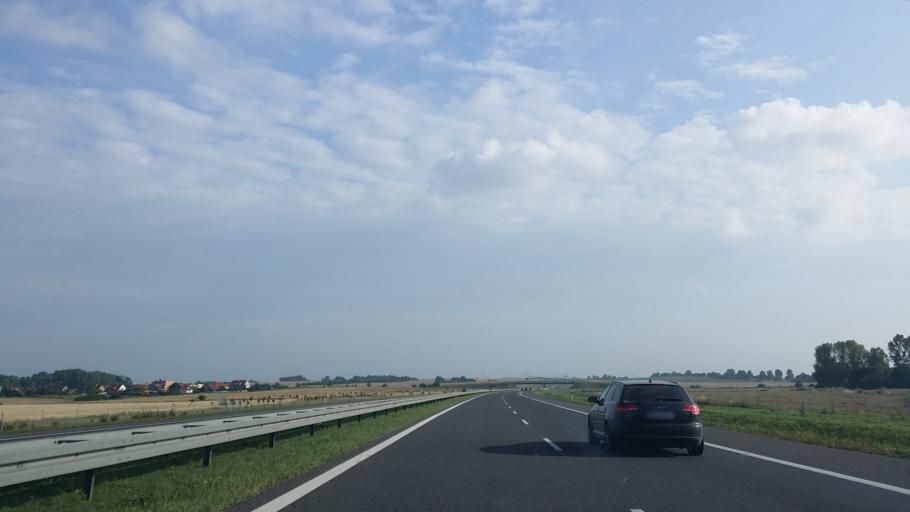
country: PL
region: Lubusz
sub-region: Powiat swiebodzinski
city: Swiebodzin
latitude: 52.2953
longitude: 15.5433
